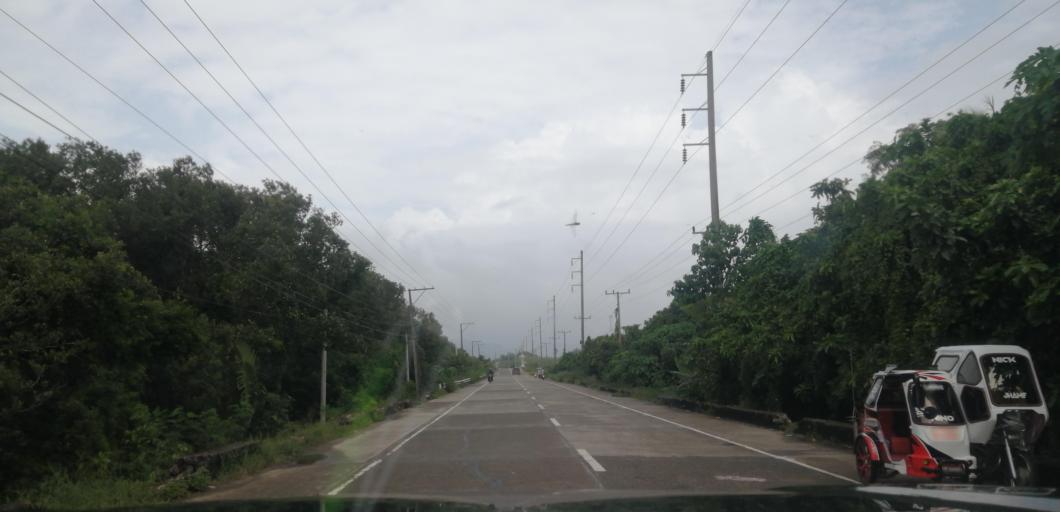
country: PH
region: Cagayan Valley
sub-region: Province of Cagayan
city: San Vicente
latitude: 18.4898
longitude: 122.1548
